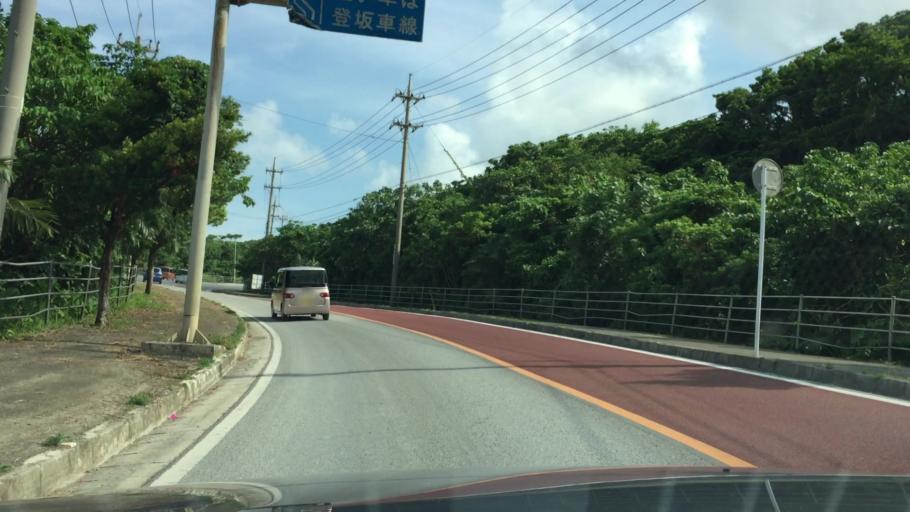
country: JP
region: Okinawa
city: Ishigaki
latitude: 24.4313
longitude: 124.2475
